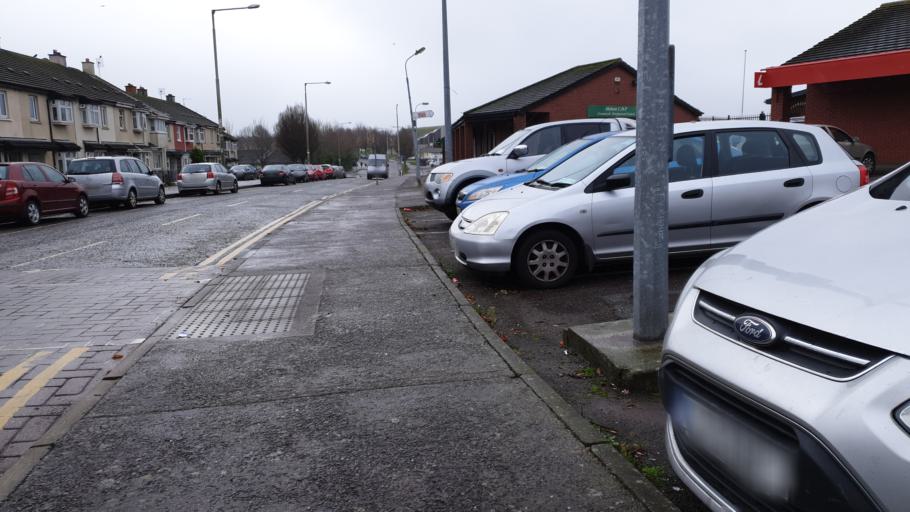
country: IE
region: Munster
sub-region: County Cork
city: Passage West
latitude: 51.8937
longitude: -8.4029
